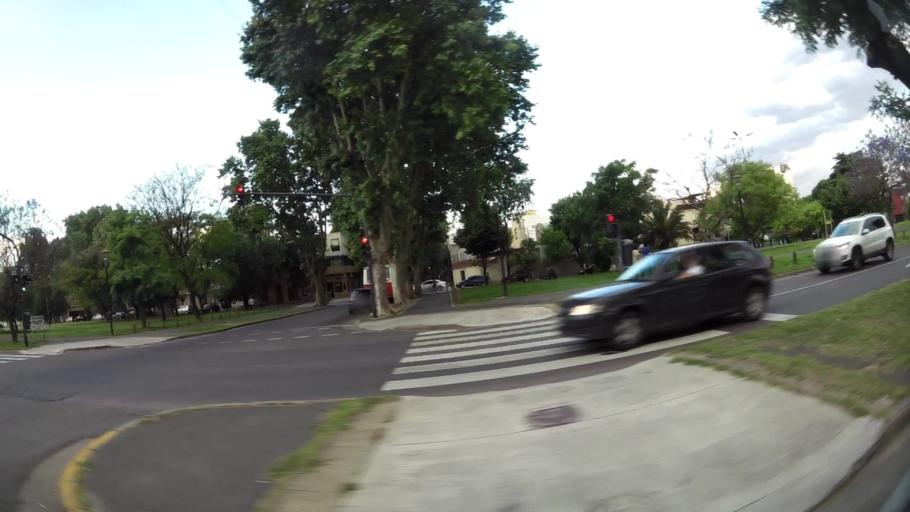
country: AR
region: Buenos Aires F.D.
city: Colegiales
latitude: -34.5634
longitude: -58.4827
